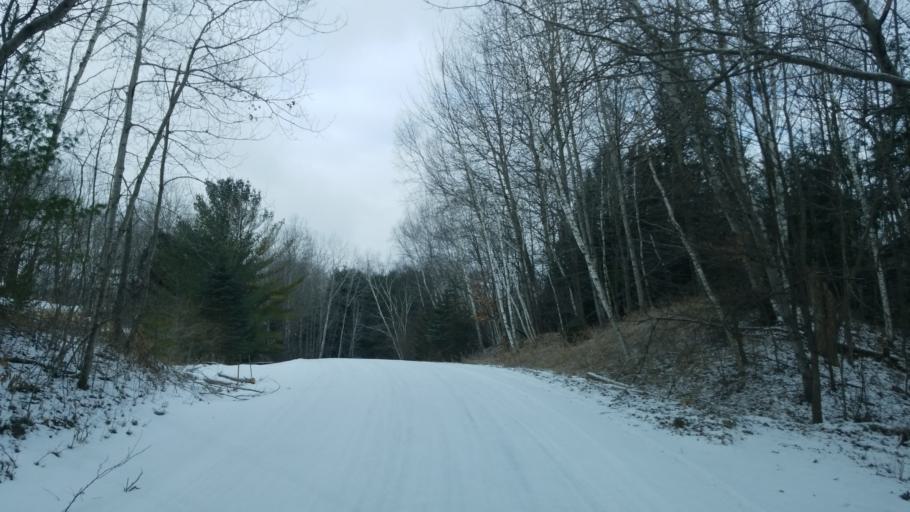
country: US
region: Michigan
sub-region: Osceola County
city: Evart
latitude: 43.8128
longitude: -85.2684
